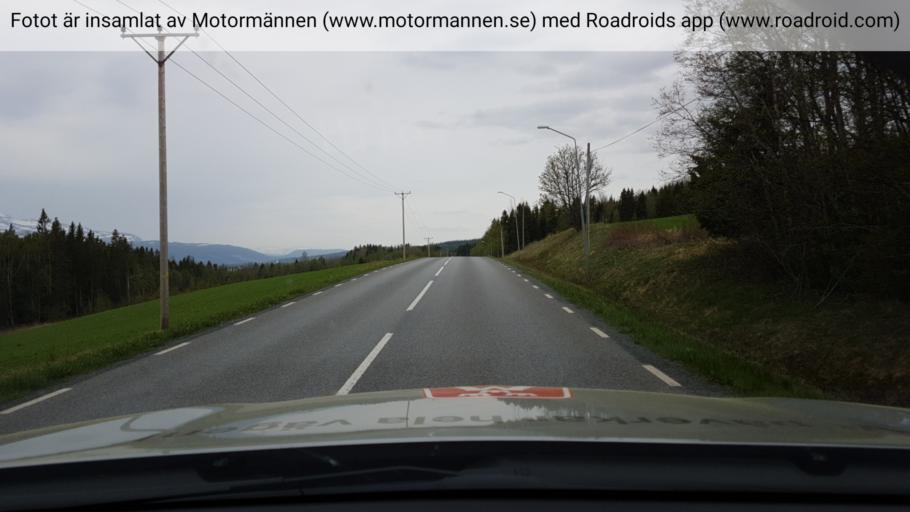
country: SE
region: Jaemtland
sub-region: Are Kommun
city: Jarpen
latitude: 63.4578
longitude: 13.3562
